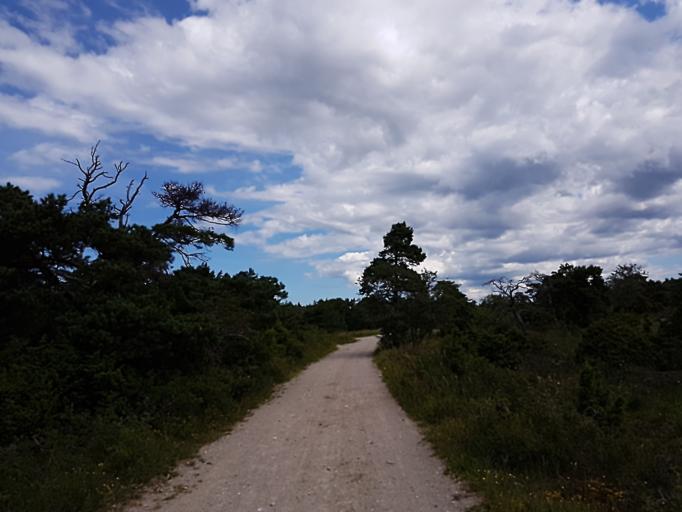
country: SE
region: Gotland
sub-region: Gotland
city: Visby
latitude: 57.6108
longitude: 18.3238
